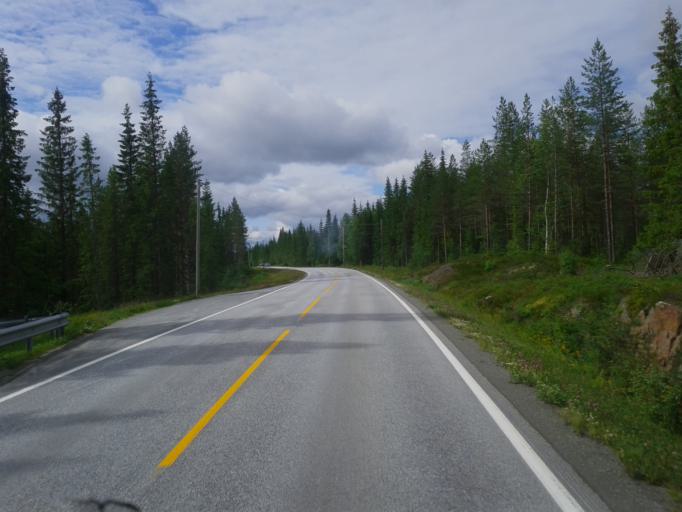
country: NO
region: Nord-Trondelag
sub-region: Hoylandet
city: Hoylandet
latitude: 64.6891
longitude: 12.7394
